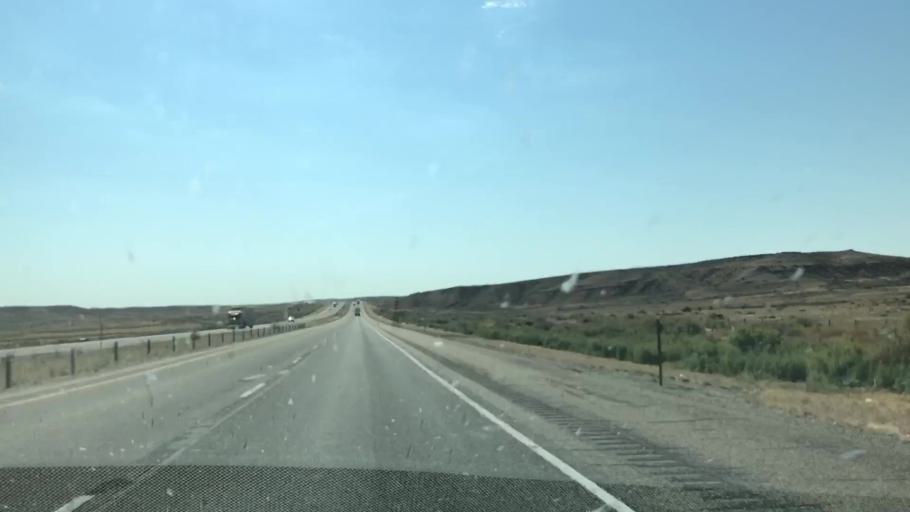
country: US
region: Wyoming
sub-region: Sweetwater County
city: Rock Springs
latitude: 41.6637
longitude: -108.7242
